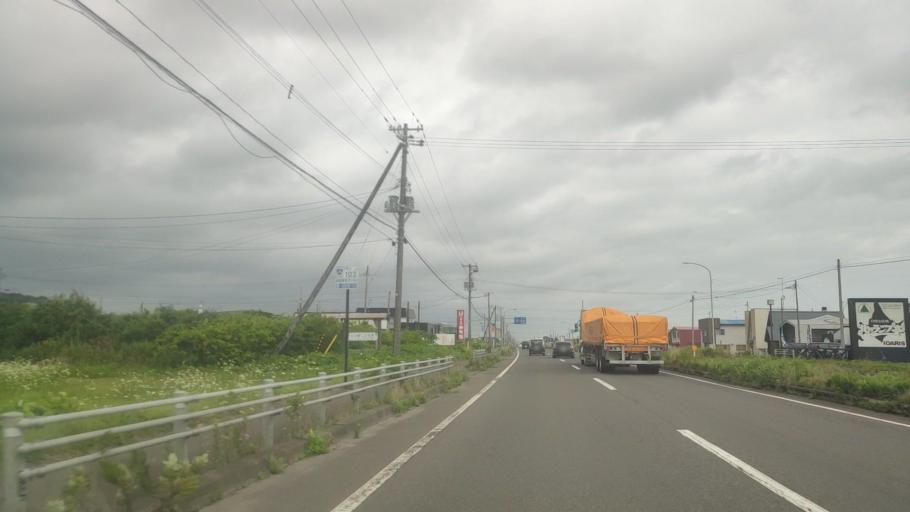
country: JP
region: Hokkaido
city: Shiraoi
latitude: 42.4751
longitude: 141.2374
